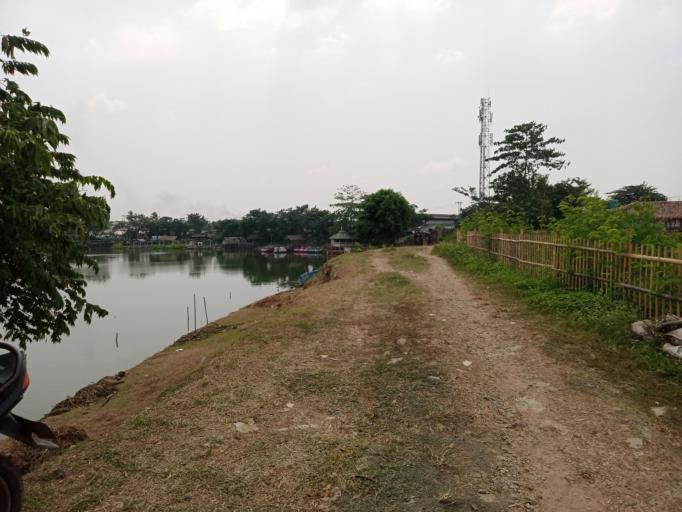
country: ID
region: West Java
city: Pasarkemis
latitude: -6.1735
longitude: 106.5410
